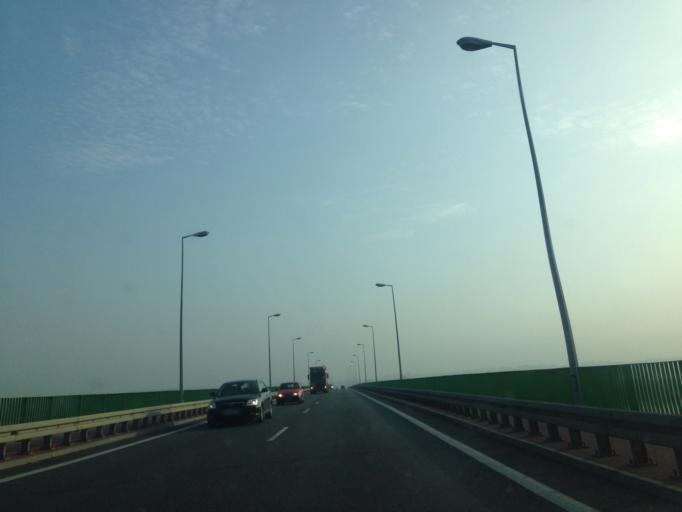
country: PL
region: Kujawsko-Pomorskie
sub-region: Powiat chelminski
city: Chelmno
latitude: 53.3719
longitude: 18.4254
